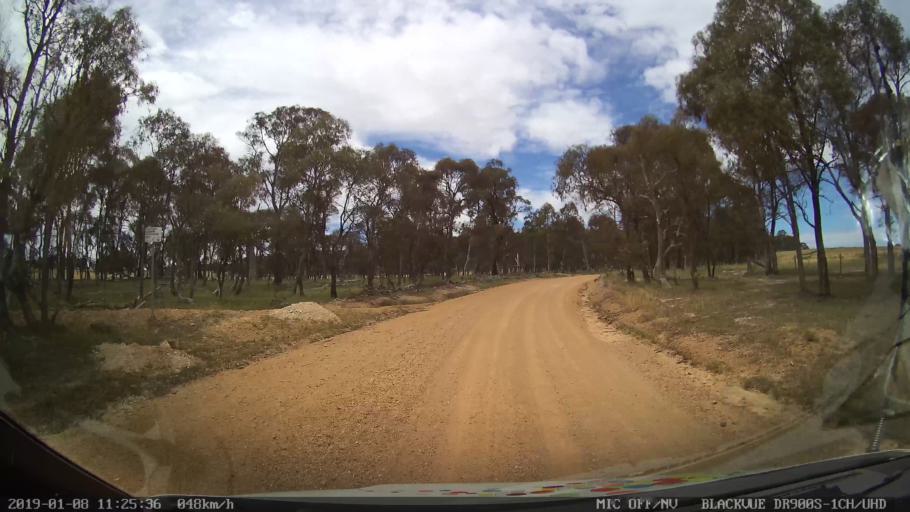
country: AU
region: New South Wales
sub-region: Guyra
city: Guyra
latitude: -30.2747
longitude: 151.5612
